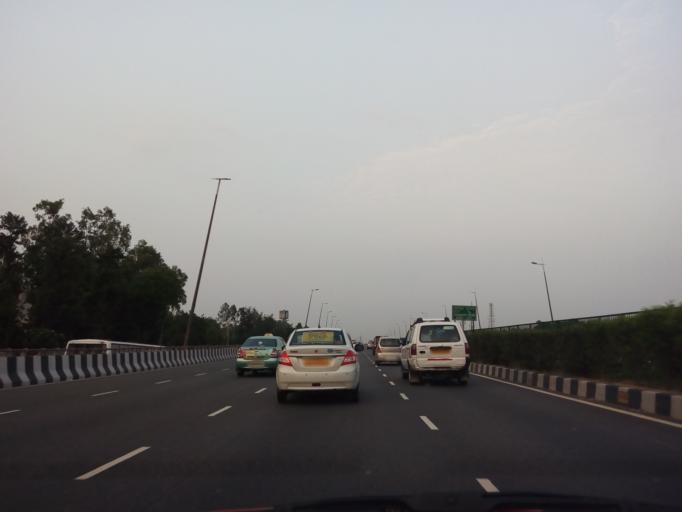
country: IN
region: Haryana
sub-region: Gurgaon
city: Gurgaon
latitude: 28.5247
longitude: 77.1004
